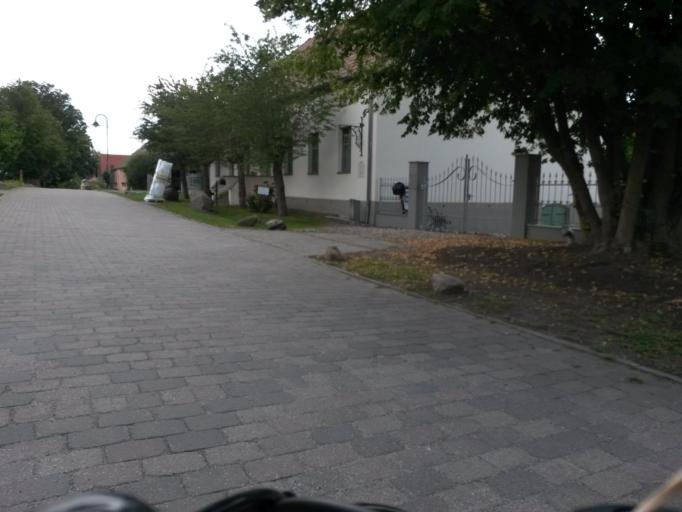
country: DE
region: Brandenburg
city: Zichow
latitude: 53.1178
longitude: 14.0154
